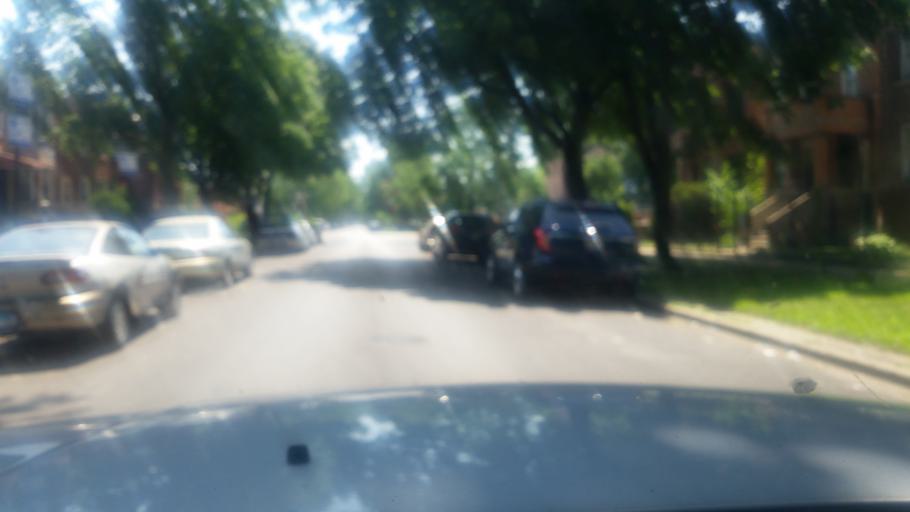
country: US
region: Illinois
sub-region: Cook County
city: Chicago
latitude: 41.7664
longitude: -87.6201
